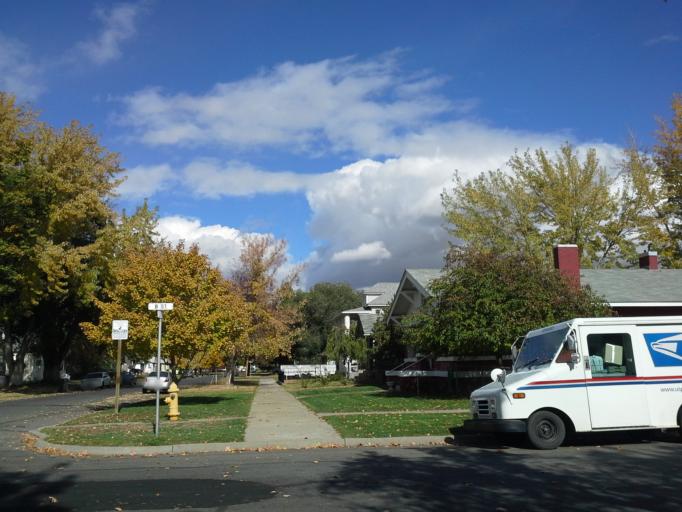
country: US
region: Oregon
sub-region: Baker County
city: Baker City
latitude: 44.7834
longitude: -117.8318
